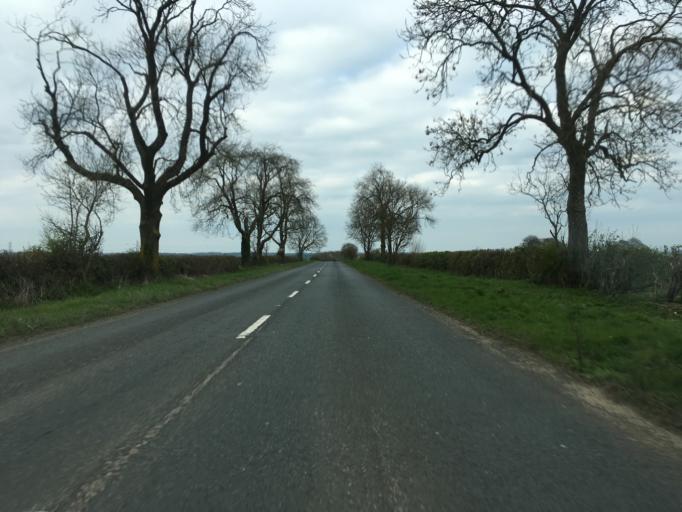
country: GB
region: England
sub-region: Gloucestershire
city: Northleach
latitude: 51.7754
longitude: -1.8004
